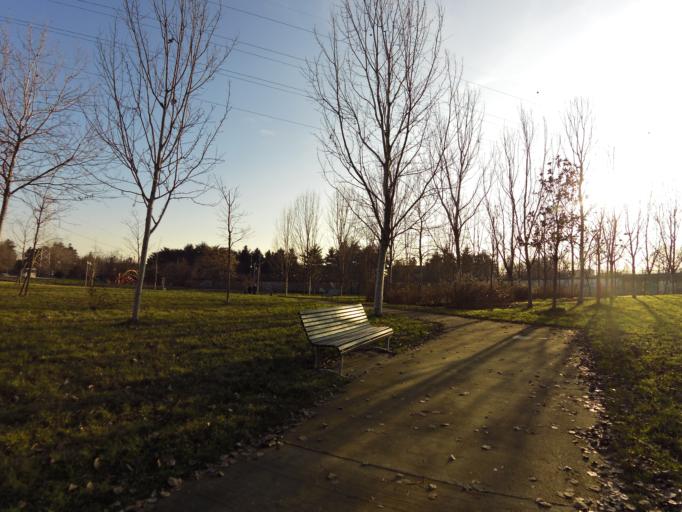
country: IT
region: Lombardy
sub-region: Citta metropolitana di Milano
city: Cologno Monzese
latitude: 45.5175
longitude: 9.2732
